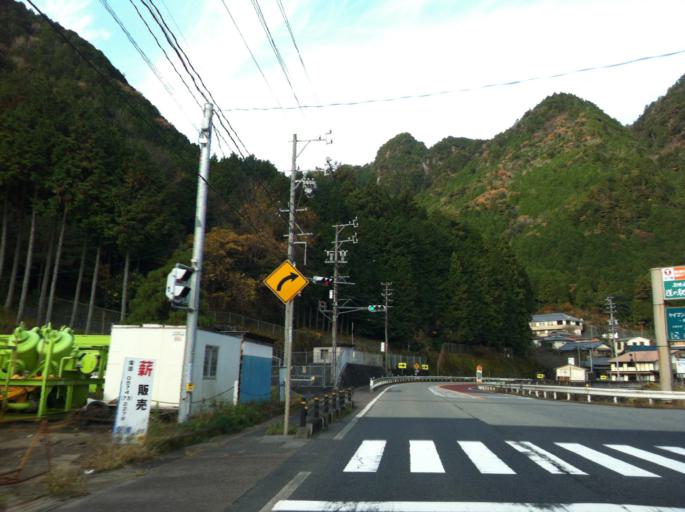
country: JP
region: Gifu
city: Minokamo
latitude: 35.5981
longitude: 137.1575
